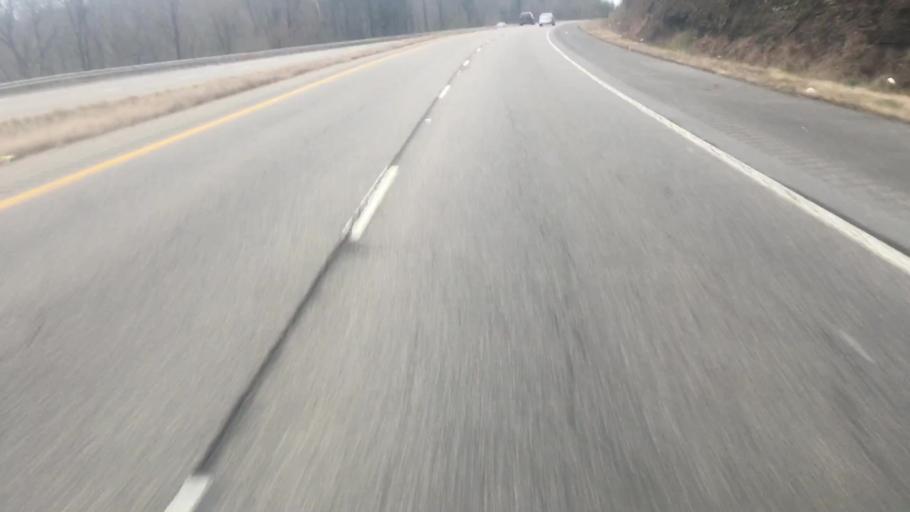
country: US
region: Alabama
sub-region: Walker County
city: Cordova
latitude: 33.8149
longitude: -87.1488
